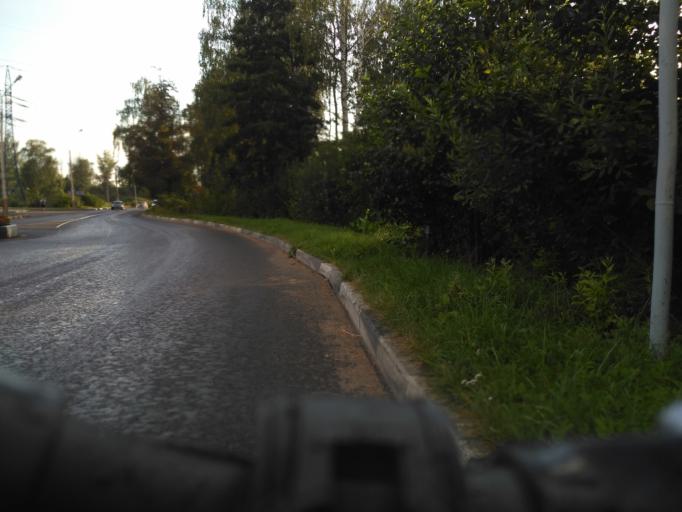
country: RU
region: Moskovskaya
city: Dubna
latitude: 56.7307
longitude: 37.1388
